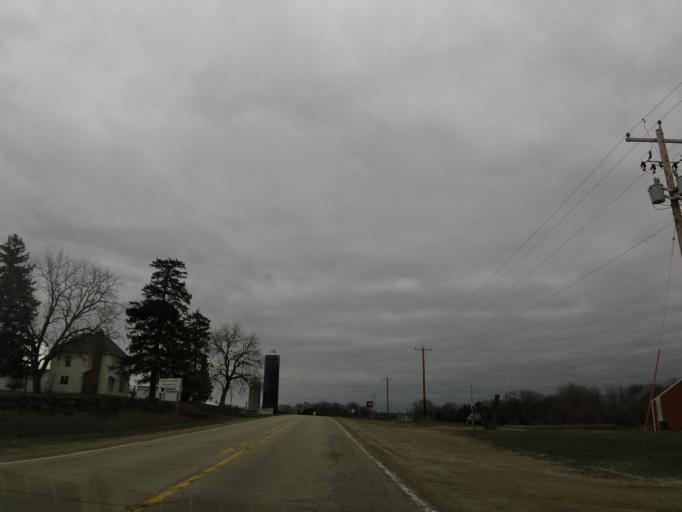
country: US
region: Iowa
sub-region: Benton County
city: Vinton
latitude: 42.3143
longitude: -91.9962
